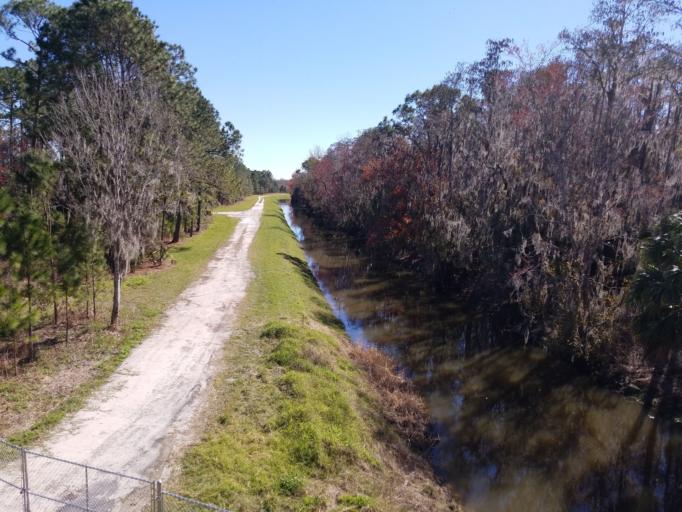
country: US
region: Florida
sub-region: Orange County
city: Tangelo Park
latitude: 28.4363
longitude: -81.4312
